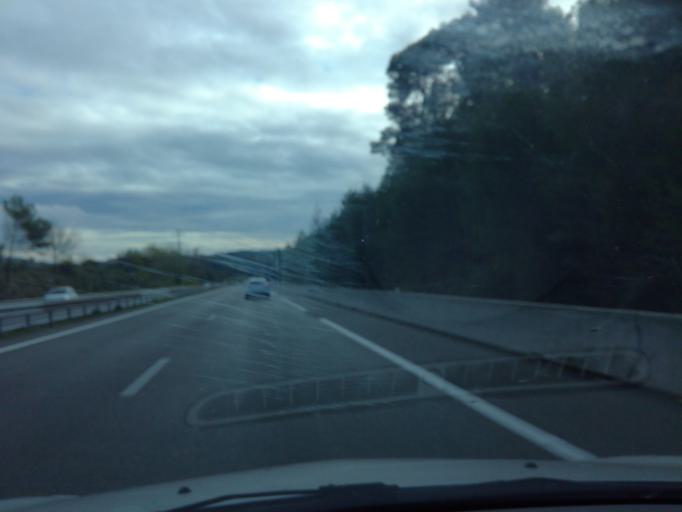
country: FR
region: Provence-Alpes-Cote d'Azur
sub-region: Departement des Alpes-Maritimes
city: Mouans-Sartoux
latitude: 43.6309
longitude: 6.9470
